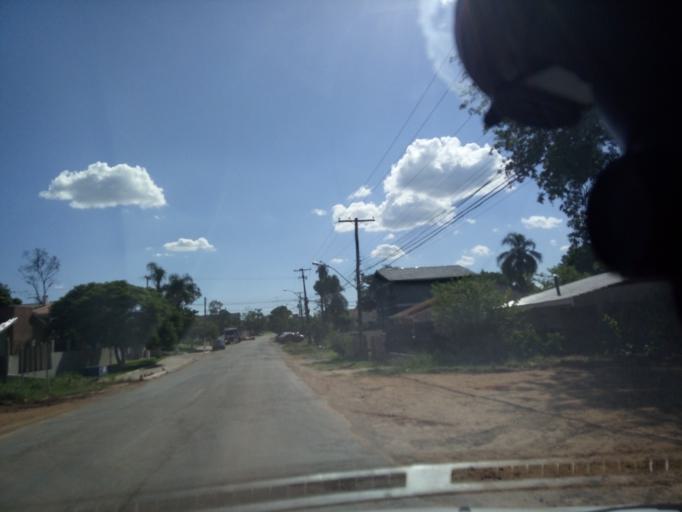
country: BR
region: Rio Grande do Sul
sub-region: Santa Maria
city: Santa Maria
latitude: -29.6981
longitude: -53.7253
